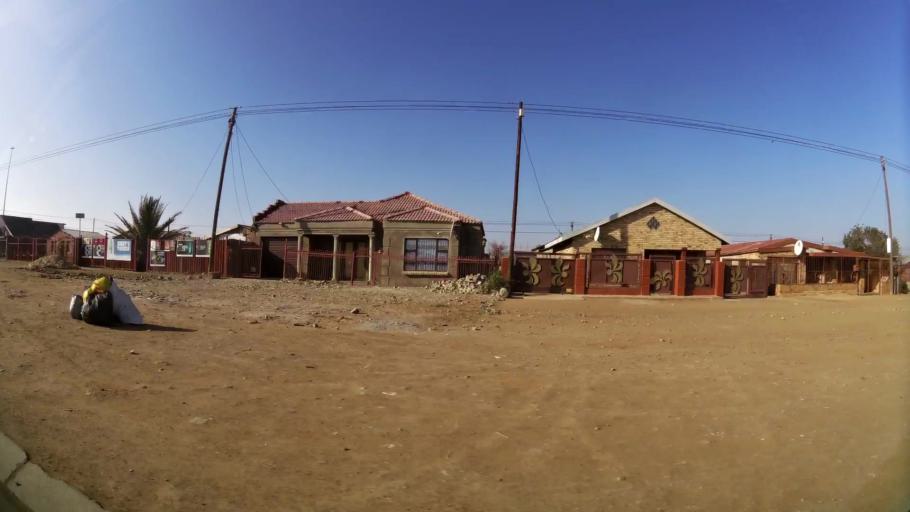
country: ZA
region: Orange Free State
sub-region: Mangaung Metropolitan Municipality
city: Bloemfontein
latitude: -29.2006
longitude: 26.2223
